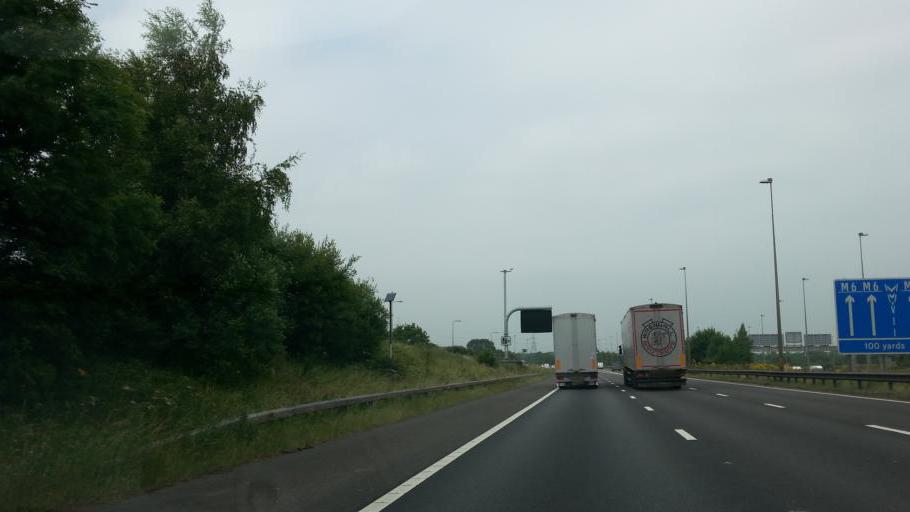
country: GB
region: England
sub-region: Staffordshire
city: Featherstone
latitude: 52.6600
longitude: -2.0653
